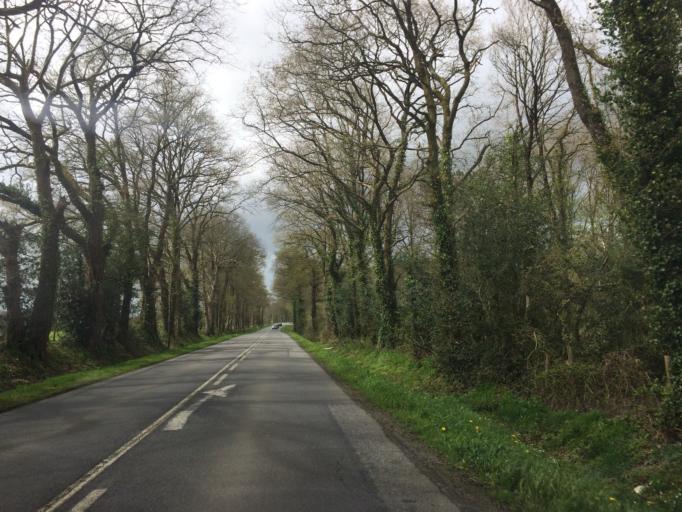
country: FR
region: Brittany
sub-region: Departement du Morbihan
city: Pluherlin
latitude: 47.6781
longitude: -2.3863
